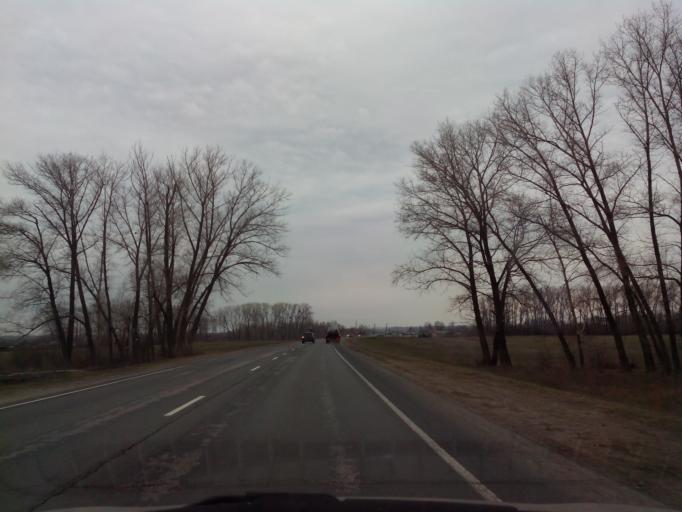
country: RU
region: Tambov
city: Zavoronezhskoye
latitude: 52.9503
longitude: 40.5844
